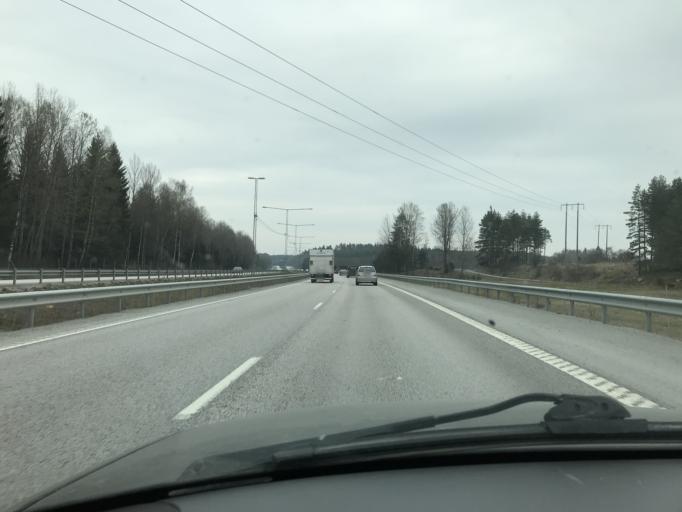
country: SE
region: Stockholm
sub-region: Taby Kommun
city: Taby
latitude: 59.4766
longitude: 18.1636
